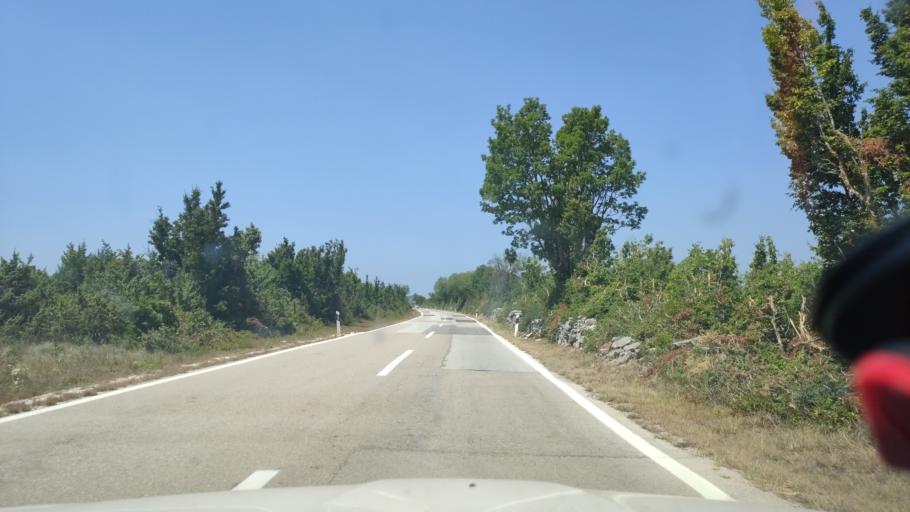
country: HR
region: Sibensko-Kniniska
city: Kistanje
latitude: 43.9768
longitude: 15.9326
